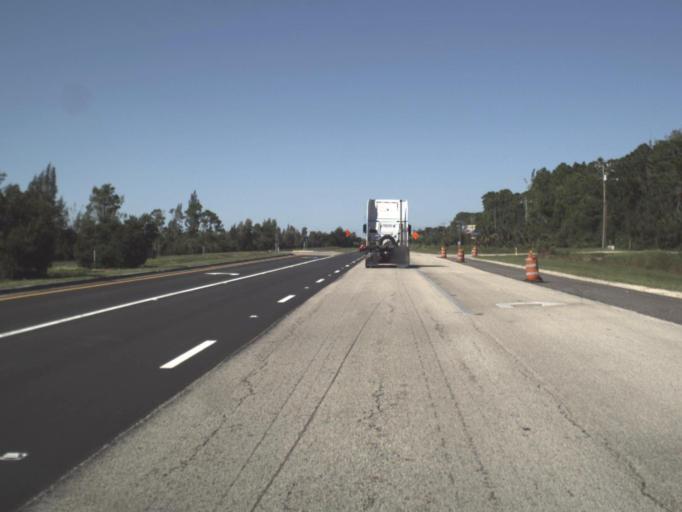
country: US
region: Florida
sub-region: Lee County
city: Suncoast Estates
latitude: 26.7593
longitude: -81.9252
